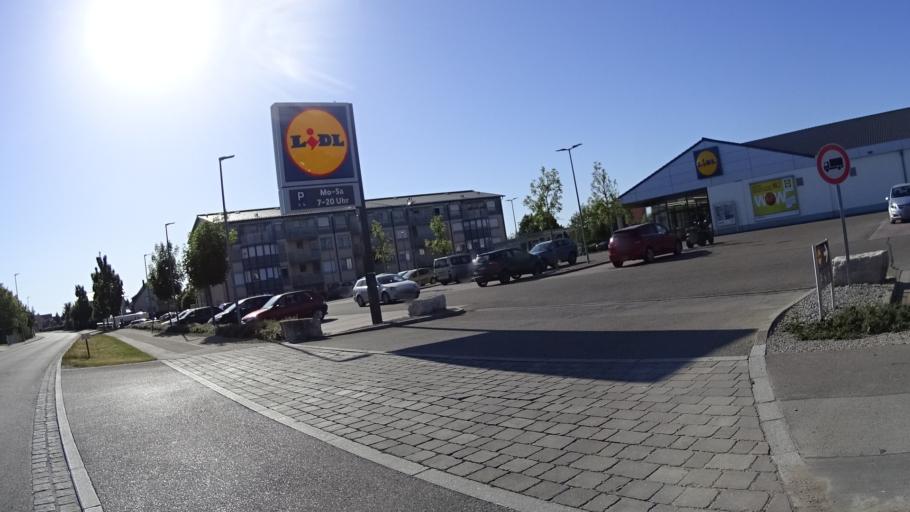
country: DE
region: Bavaria
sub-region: Regierungsbezirk Mittelfranken
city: Arberg
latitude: 49.1580
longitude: 10.5568
